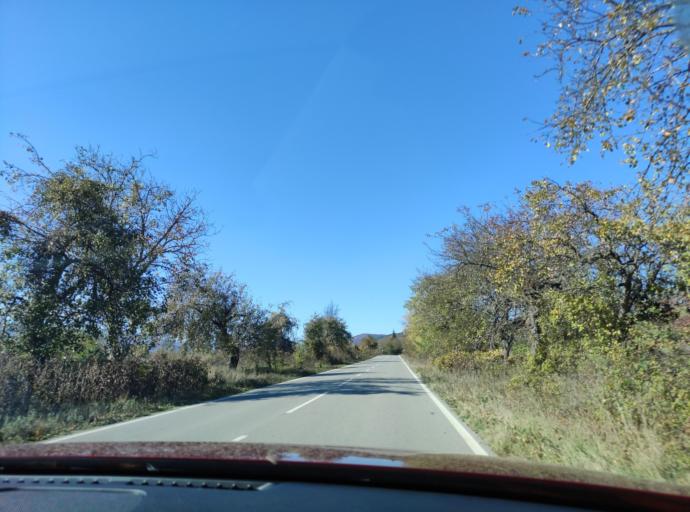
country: BG
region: Montana
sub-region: Obshtina Chiprovtsi
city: Chiprovtsi
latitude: 43.4207
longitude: 23.0195
